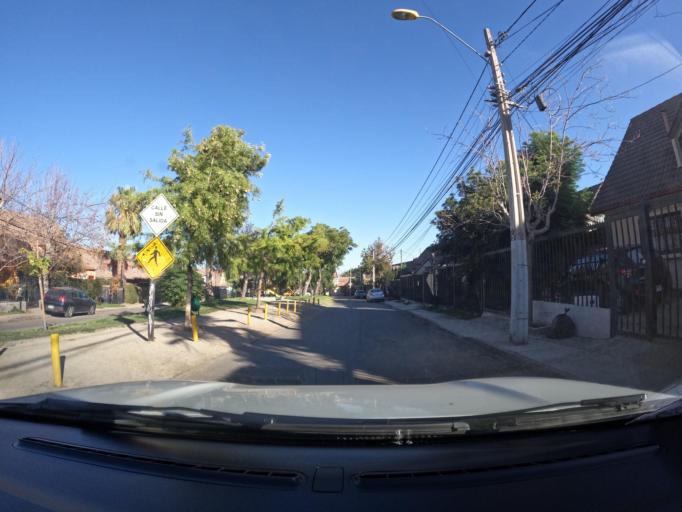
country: CL
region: Santiago Metropolitan
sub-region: Provincia de Santiago
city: Villa Presidente Frei, Nunoa, Santiago, Chile
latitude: -33.4799
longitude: -70.5486
